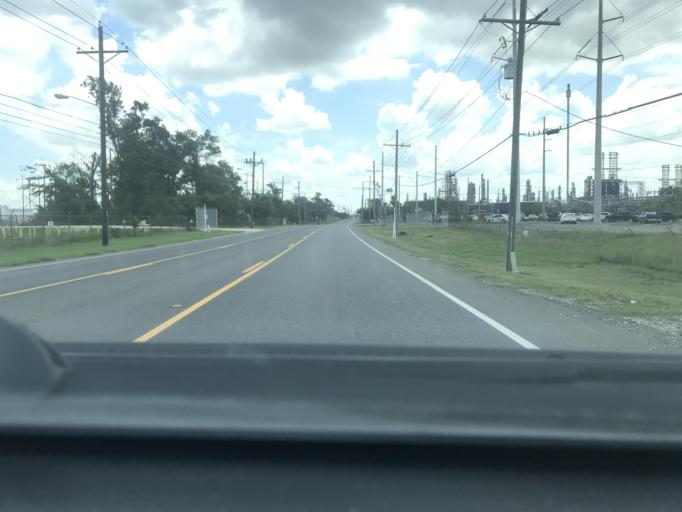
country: US
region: Louisiana
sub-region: Calcasieu Parish
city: Westlake
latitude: 30.2462
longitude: -93.2851
